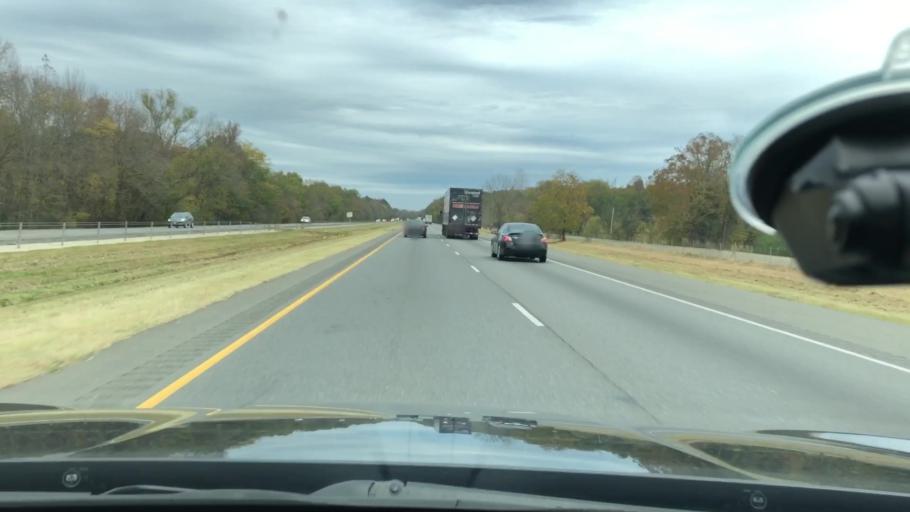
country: US
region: Arkansas
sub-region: Hot Spring County
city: Malvern
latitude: 34.3622
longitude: -92.8732
